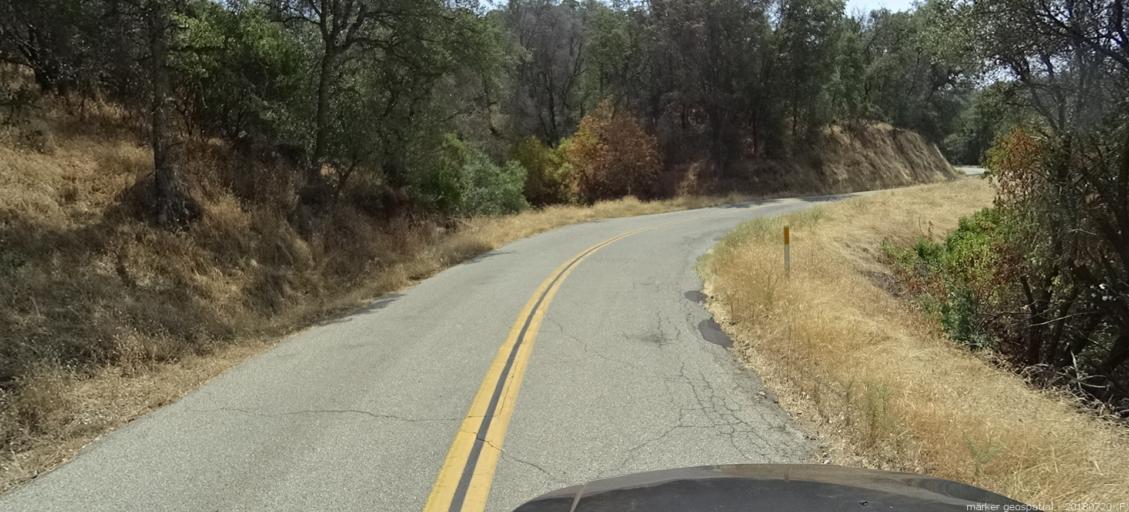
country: US
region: California
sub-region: Madera County
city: Ahwahnee
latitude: 37.3296
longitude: -119.7705
